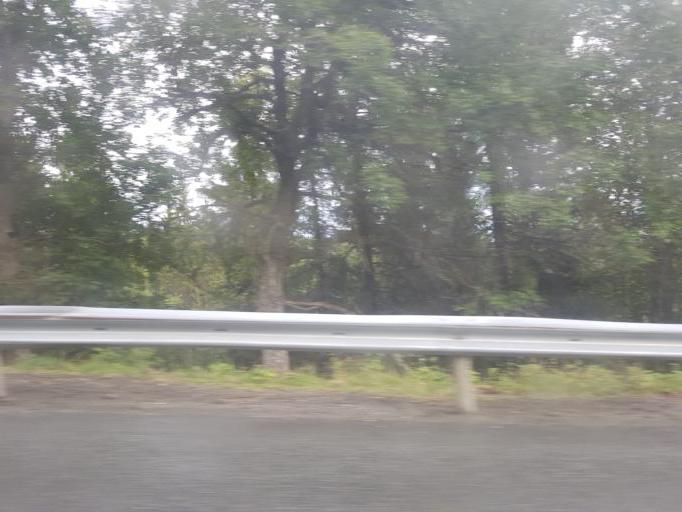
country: NO
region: Sor-Trondelag
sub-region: Trondheim
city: Trondheim
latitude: 63.4165
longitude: 10.2931
